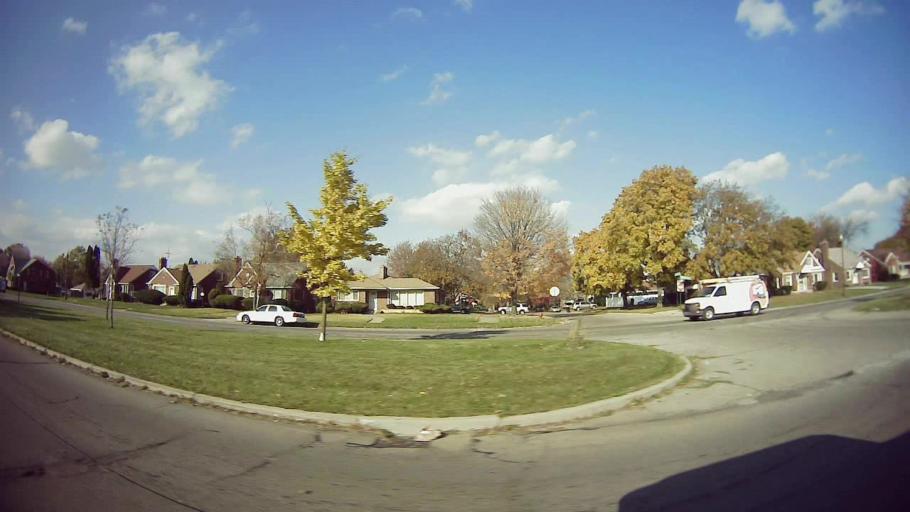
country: US
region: Michigan
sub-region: Macomb County
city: Warren
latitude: 42.4410
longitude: -83.0283
